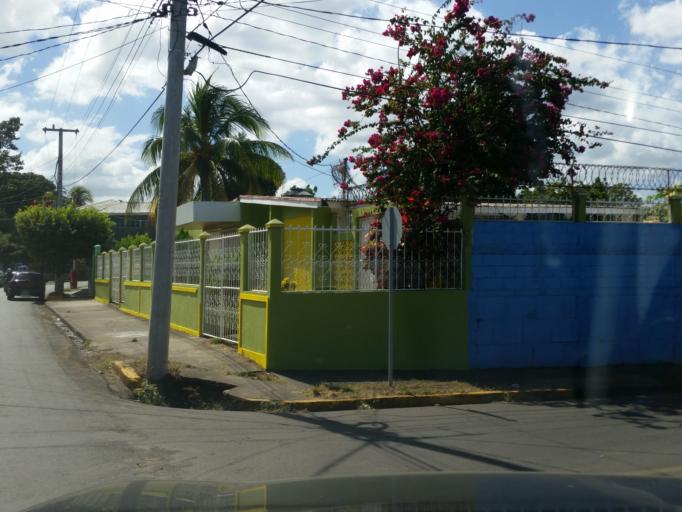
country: NI
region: Managua
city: Managua
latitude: 12.1199
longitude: -86.2294
